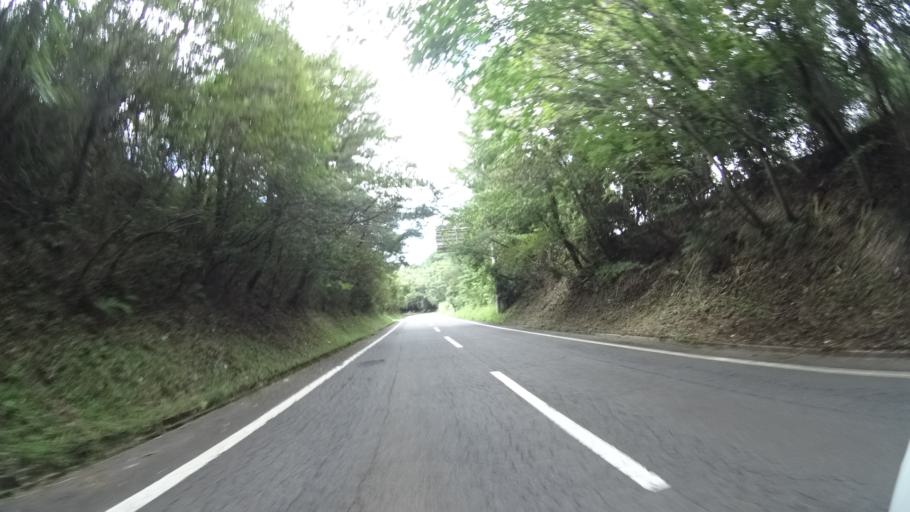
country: JP
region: Oita
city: Beppu
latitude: 33.3434
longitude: 131.4284
